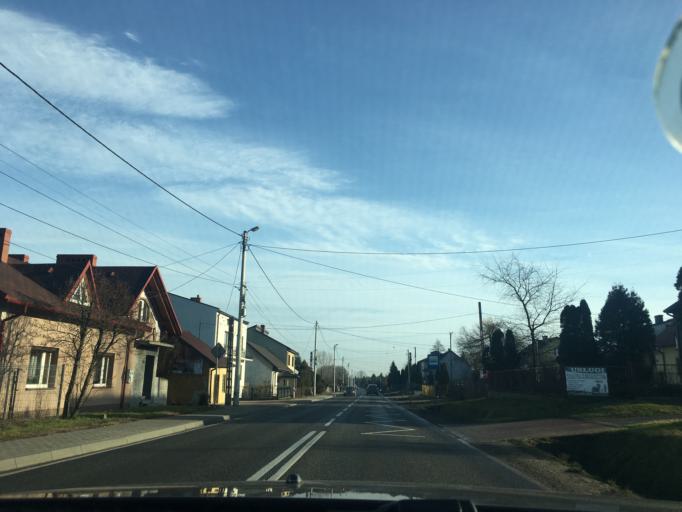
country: PL
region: Swietokrzyskie
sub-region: Powiat jedrzejowski
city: Jedrzejow
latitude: 50.6324
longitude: 20.3230
